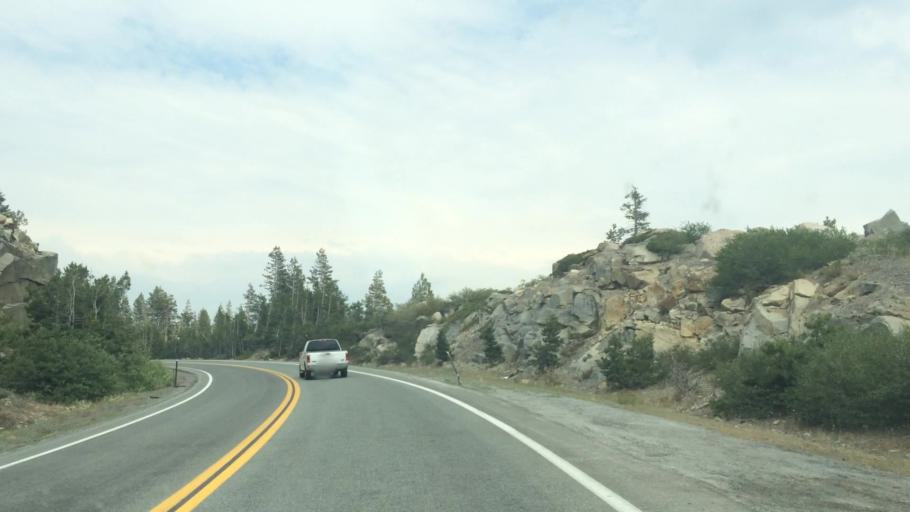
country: US
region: California
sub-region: El Dorado County
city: South Lake Tahoe
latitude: 38.6251
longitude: -120.1969
